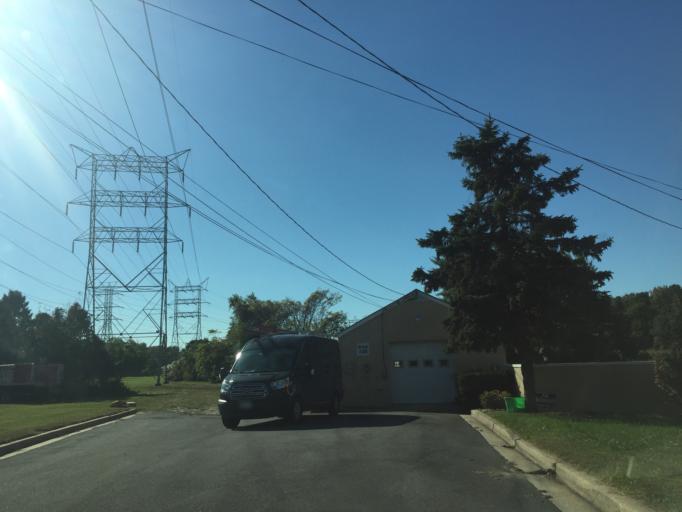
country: US
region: Maryland
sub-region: Baltimore County
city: Dundalk
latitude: 39.2554
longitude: -76.5027
